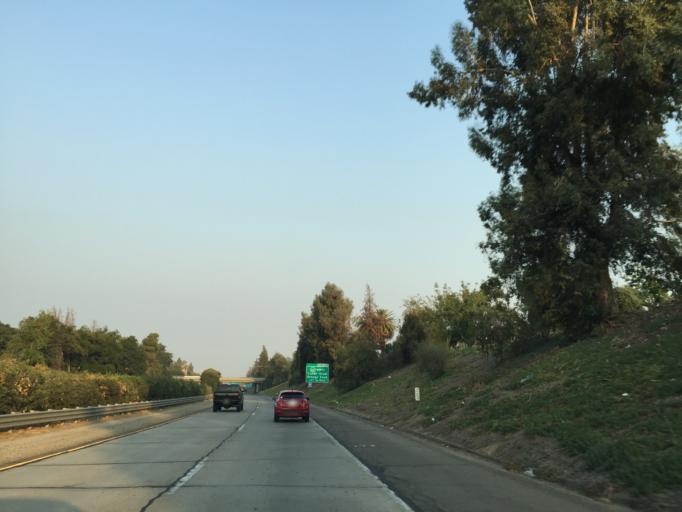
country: US
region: California
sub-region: Tulare County
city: Visalia
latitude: 36.3270
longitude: -119.2801
